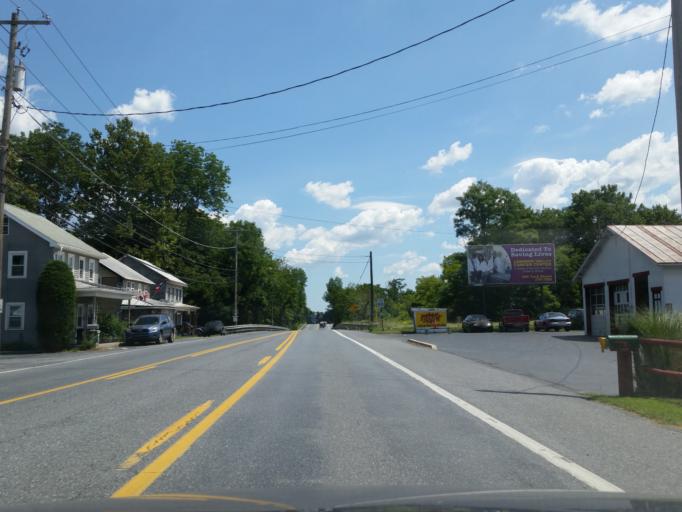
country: US
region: Pennsylvania
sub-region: Lebanon County
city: Annville
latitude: 40.3256
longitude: -76.5339
